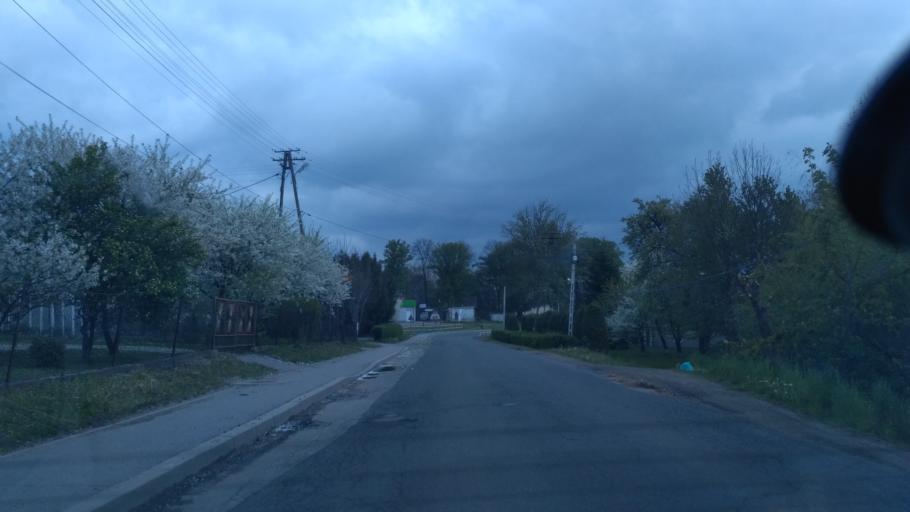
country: PL
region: Subcarpathian Voivodeship
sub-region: Powiat brzozowski
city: Jasionow
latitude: 49.6450
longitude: 21.9436
